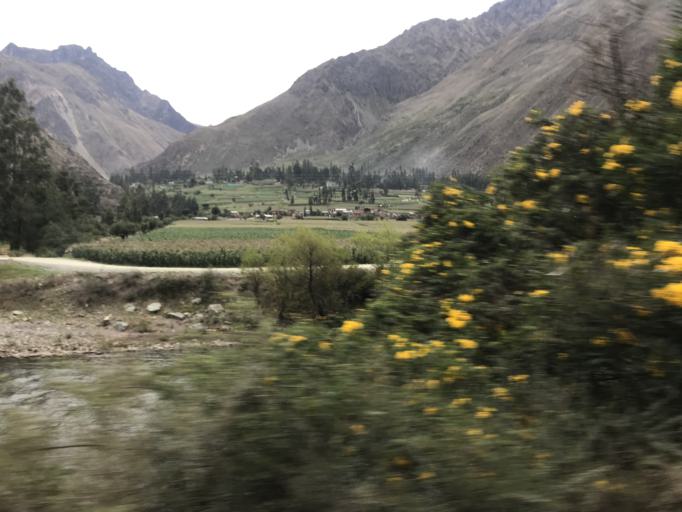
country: PE
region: Cusco
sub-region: Provincia de Urubamba
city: Ollantaytambo
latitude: -13.2242
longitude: -72.3293
